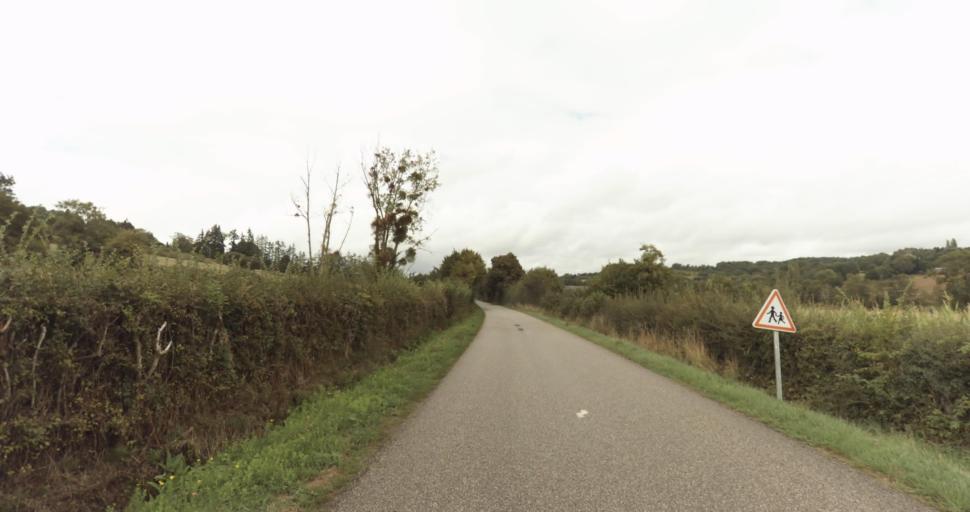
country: FR
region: Lower Normandy
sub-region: Departement de l'Orne
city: Vimoutiers
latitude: 48.8605
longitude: 0.2216
